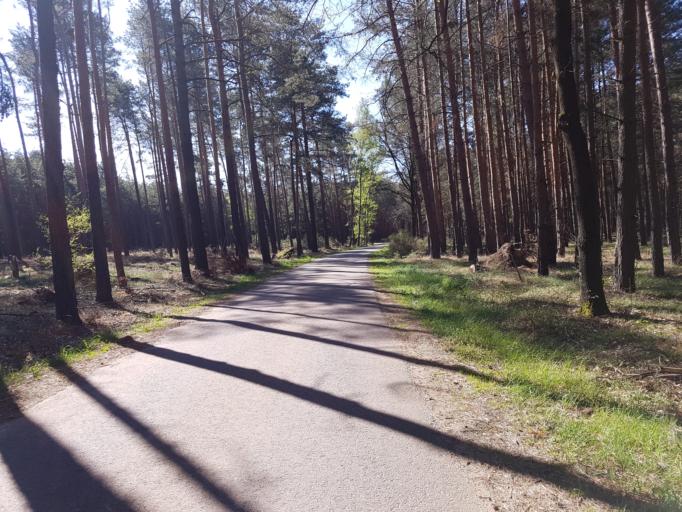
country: DE
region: Brandenburg
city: Groden
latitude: 51.3877
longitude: 13.5560
